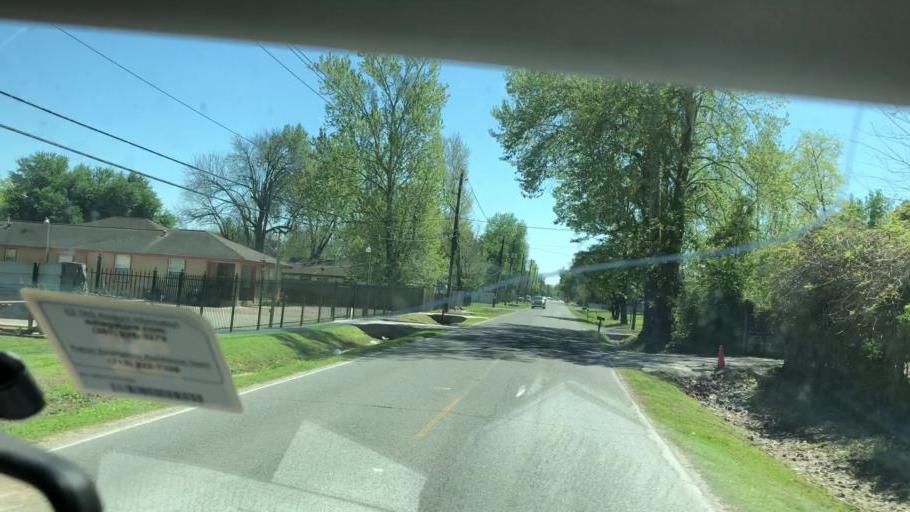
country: US
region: Texas
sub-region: Harris County
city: Aldine
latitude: 29.9062
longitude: -95.3910
